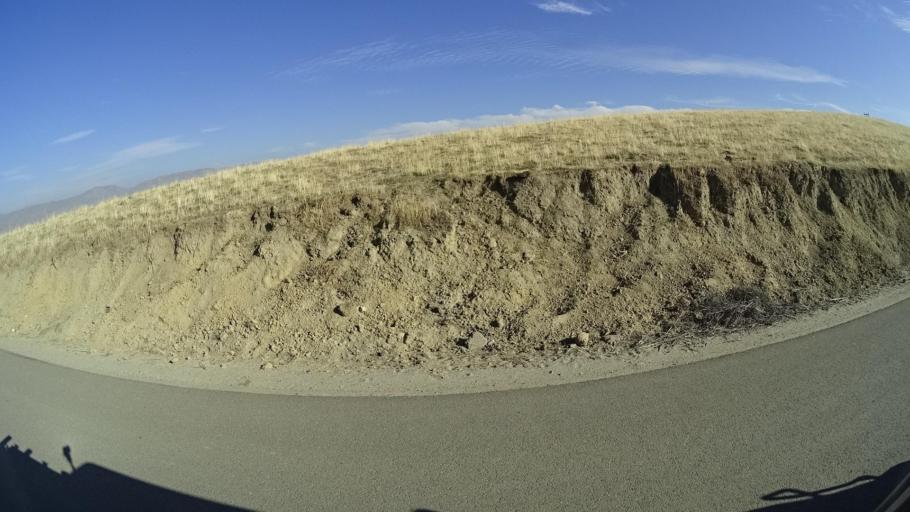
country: US
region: California
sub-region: Kern County
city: Oildale
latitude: 35.4858
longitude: -118.8761
